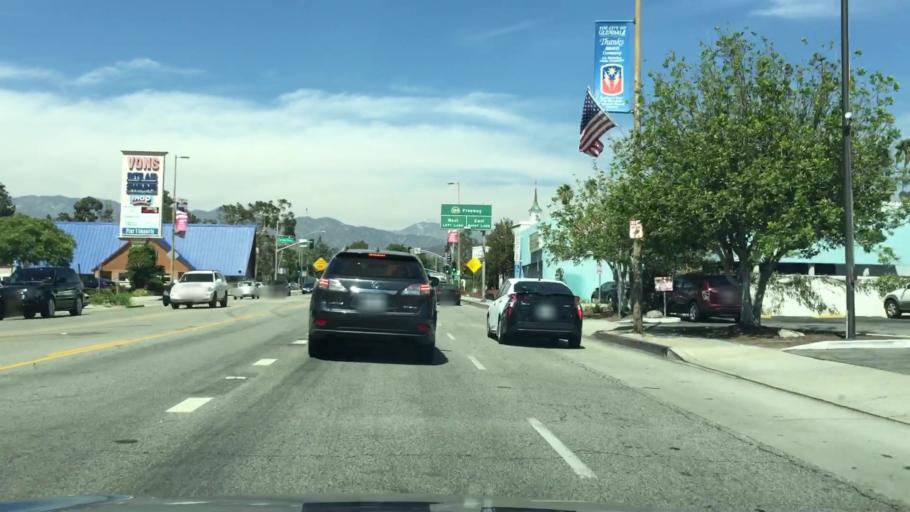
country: US
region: California
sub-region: Los Angeles County
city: Glendale
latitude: 34.1540
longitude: -118.2433
